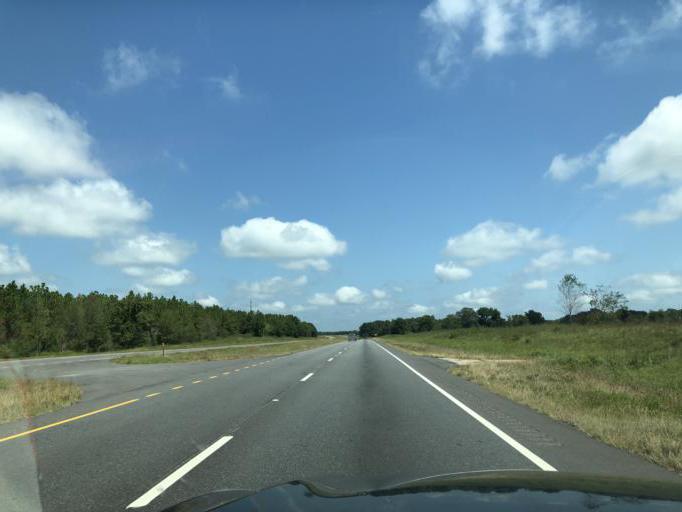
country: US
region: Alabama
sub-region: Henry County
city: Abbeville
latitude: 31.4963
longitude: -85.2943
